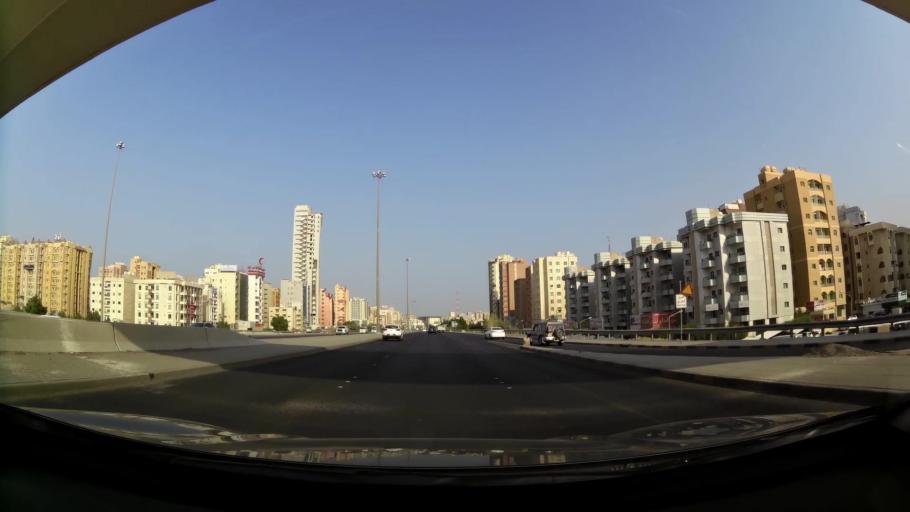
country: KW
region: Muhafazat Hawalli
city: Hawalli
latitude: 29.3311
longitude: 48.0414
